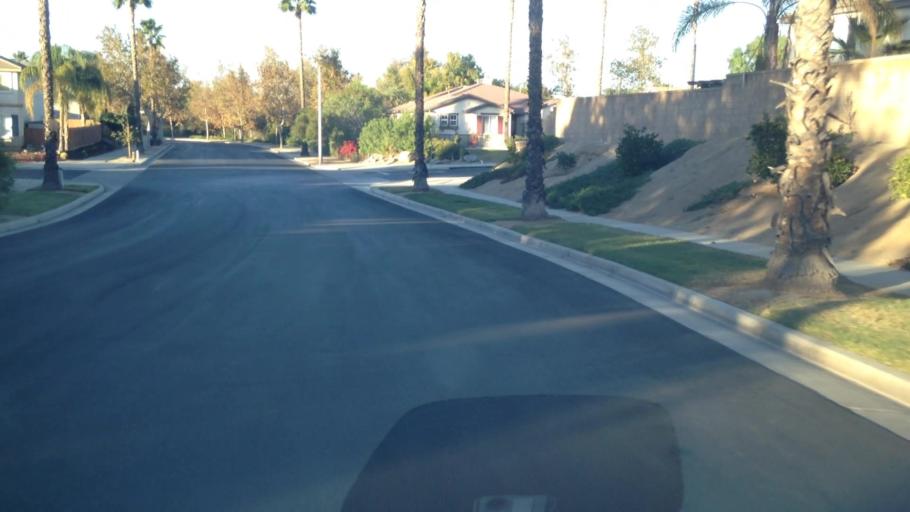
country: US
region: California
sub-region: Riverside County
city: Home Gardens
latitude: 33.8602
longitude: -117.4415
